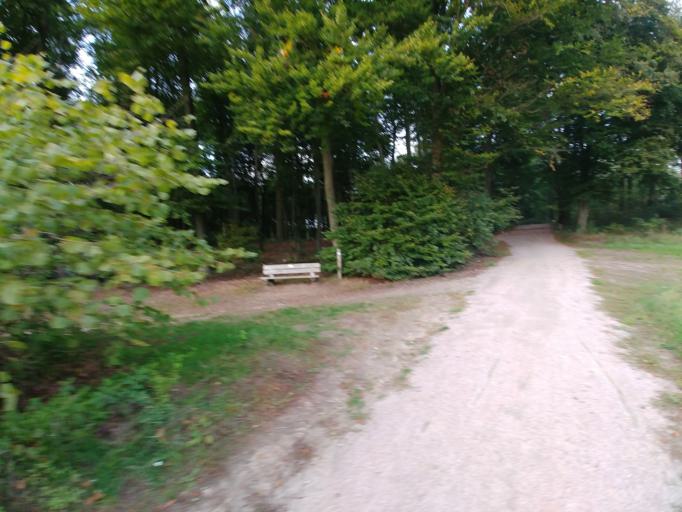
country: NL
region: Gelderland
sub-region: Gemeente Renkum
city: Doorwerth
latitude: 51.9784
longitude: 5.8133
